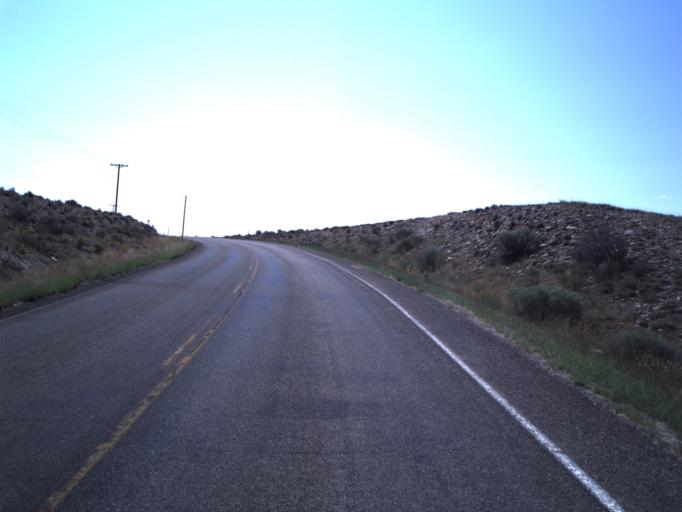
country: US
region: Utah
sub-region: Duchesne County
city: Duchesne
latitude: 40.2506
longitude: -110.3977
